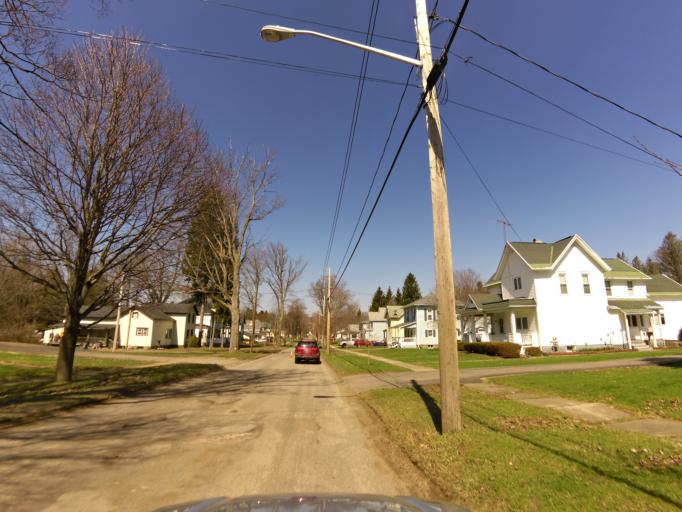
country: US
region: New York
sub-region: Cattaraugus County
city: Franklinville
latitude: 42.3341
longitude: -78.4474
